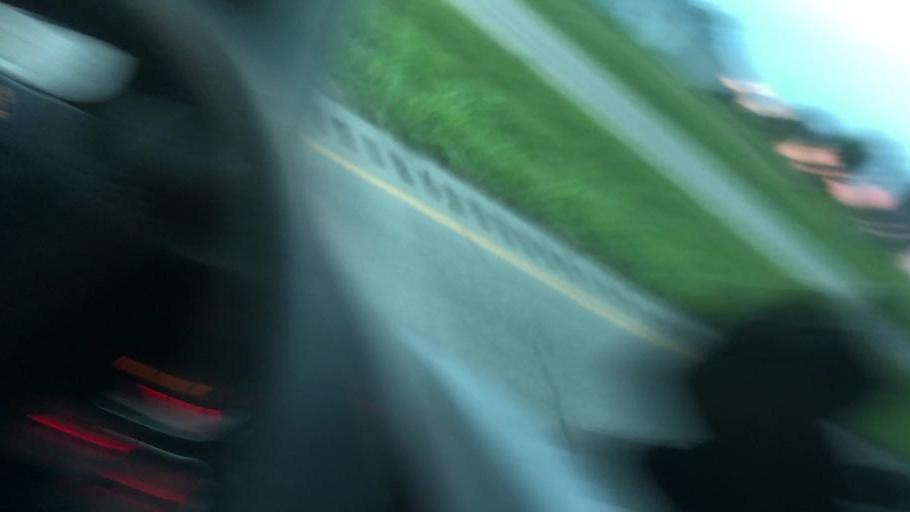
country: US
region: Oklahoma
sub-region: Kay County
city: Ponca City
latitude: 36.7808
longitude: -97.0672
